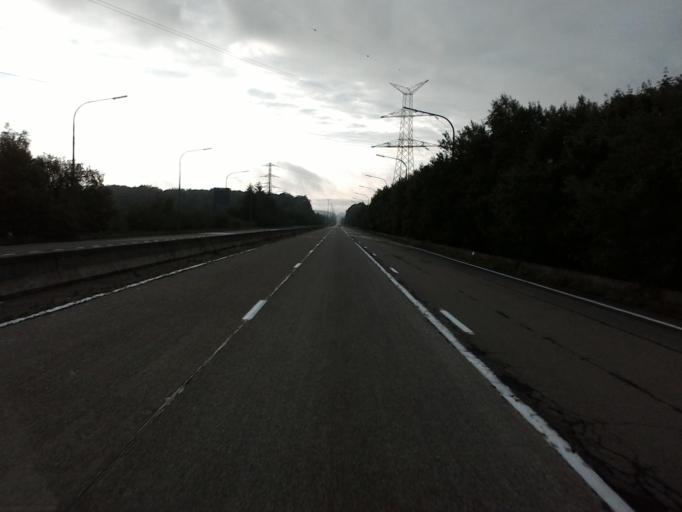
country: BE
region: Wallonia
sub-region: Province du Luxembourg
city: Attert
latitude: 49.7802
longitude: 5.7530
